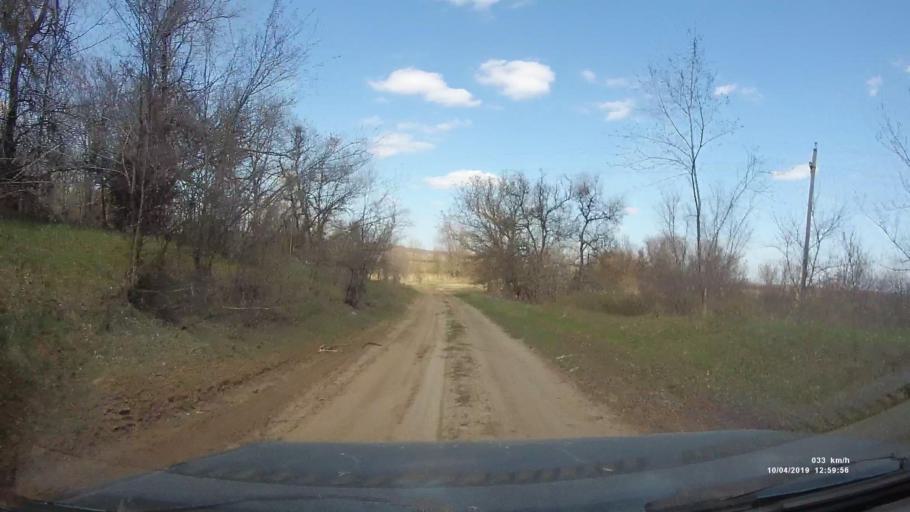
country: RU
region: Rostov
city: Masalovka
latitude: 48.3795
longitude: 40.2293
